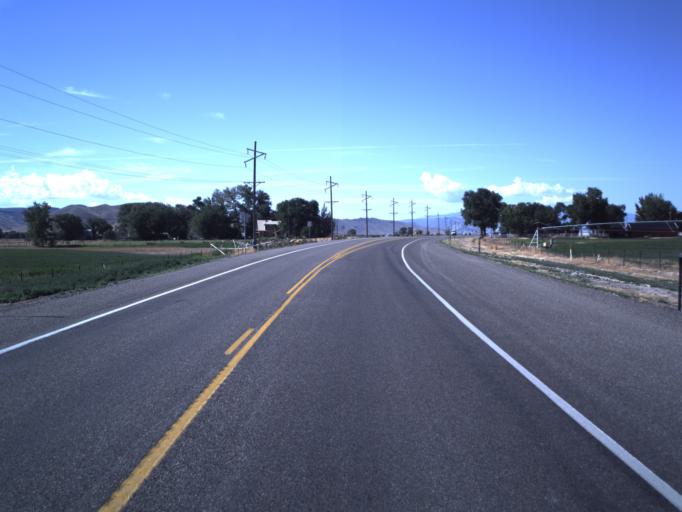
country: US
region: Utah
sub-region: Sanpete County
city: Centerfield
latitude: 39.0590
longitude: -111.8208
